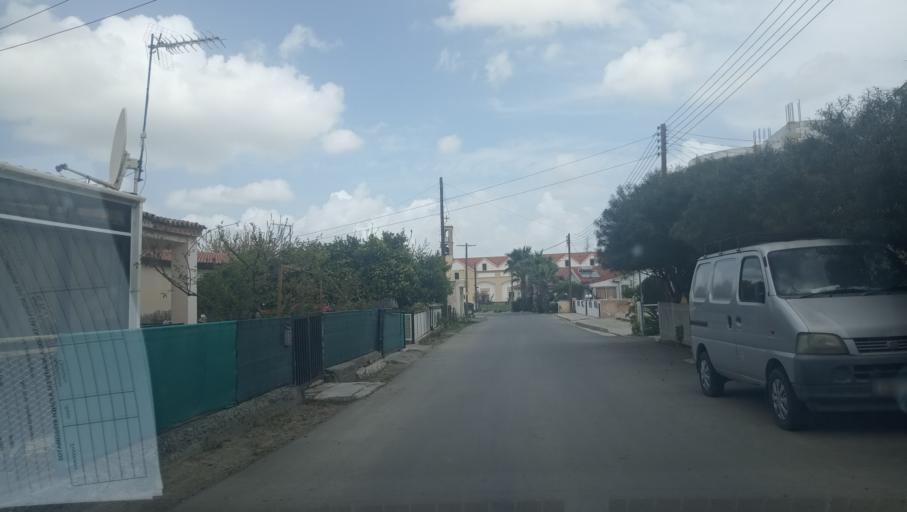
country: CY
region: Lefkosia
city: Kato Deftera
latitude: 35.0820
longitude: 33.2709
